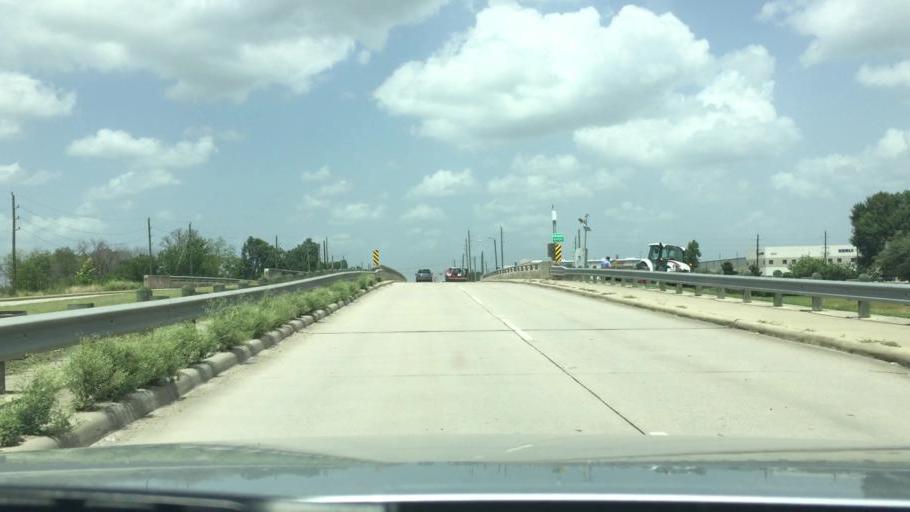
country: US
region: Texas
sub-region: Harris County
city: Hudson
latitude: 29.9486
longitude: -95.5192
